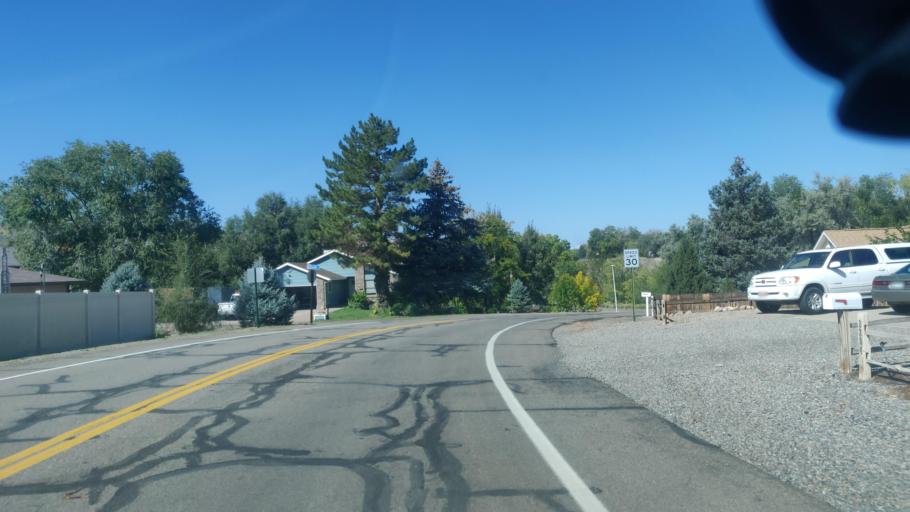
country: US
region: Colorado
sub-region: Mesa County
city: Redlands
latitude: 39.0820
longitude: -108.6267
